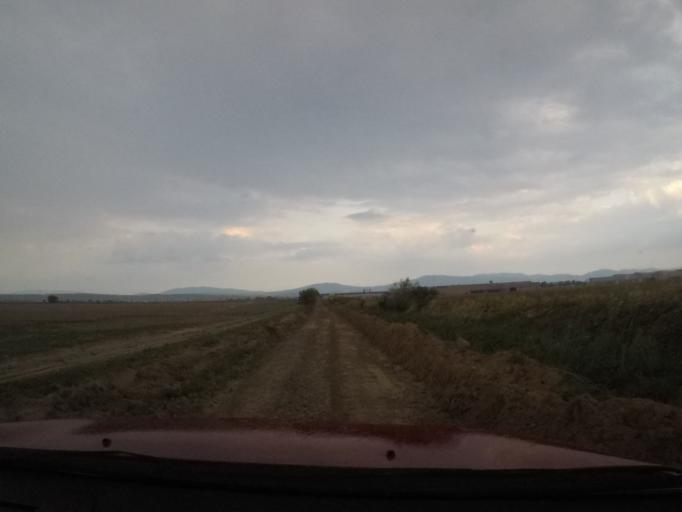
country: SK
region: Kosicky
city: Kosice
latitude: 48.6806
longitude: 21.2227
